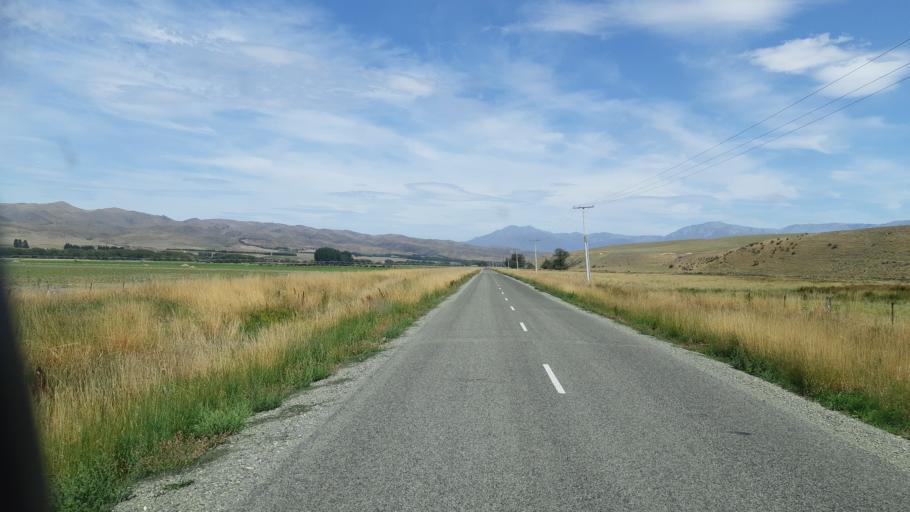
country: NZ
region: Otago
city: Oamaru
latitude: -44.6438
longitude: 170.6062
